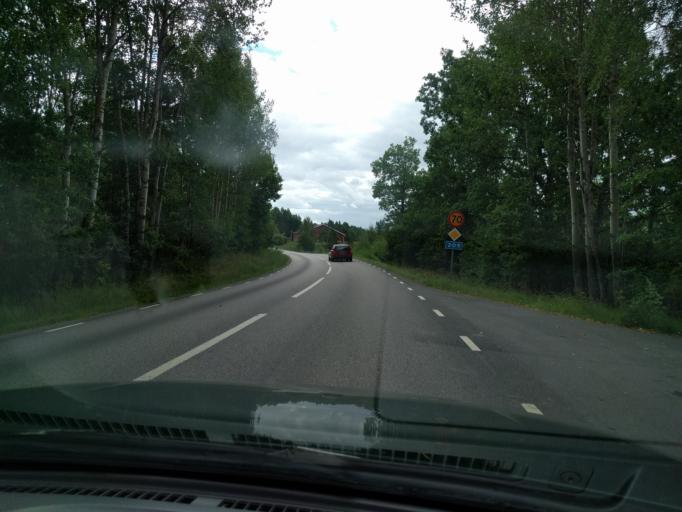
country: SE
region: Soedermanland
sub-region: Nykopings Kommun
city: Svalsta
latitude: 58.5342
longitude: 16.7435
